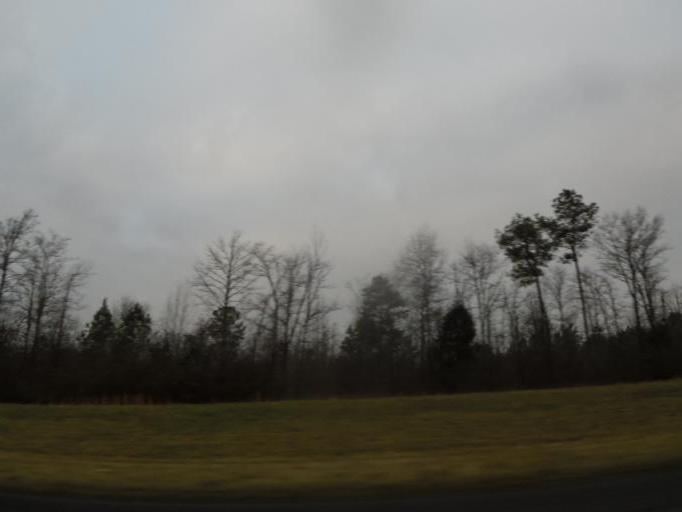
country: US
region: Alabama
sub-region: Blount County
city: Smoke Rise
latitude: 33.9262
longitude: -86.8673
